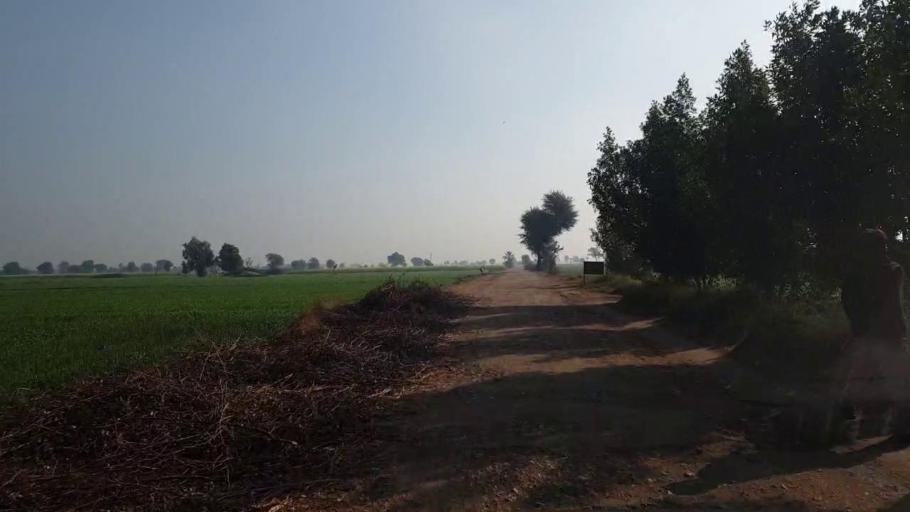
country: PK
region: Sindh
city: Shahdadpur
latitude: 26.0004
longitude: 68.6133
